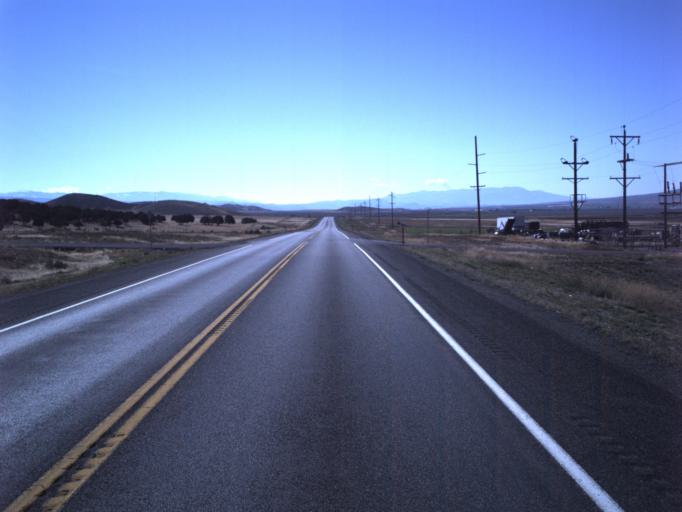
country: US
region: Utah
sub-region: Sanpete County
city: Gunnison
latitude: 39.2236
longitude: -111.8481
